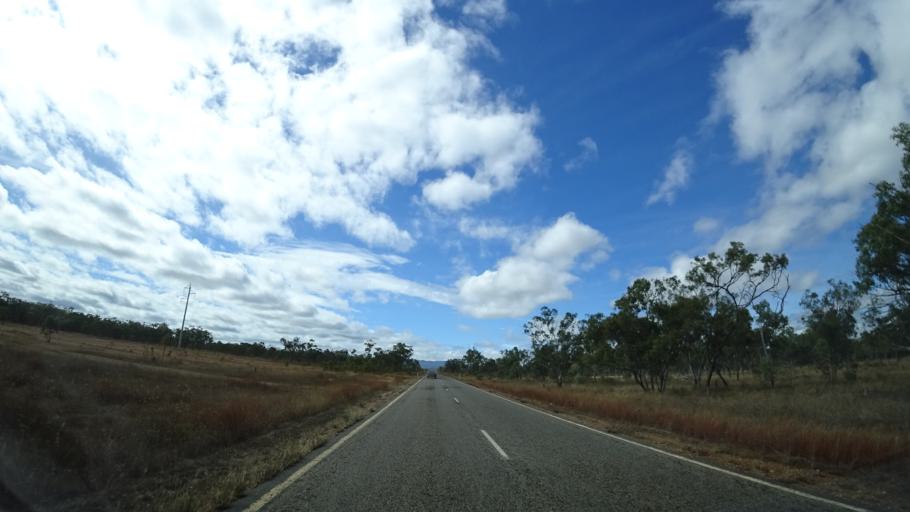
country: AU
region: Queensland
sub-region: Cairns
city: Port Douglas
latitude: -16.4972
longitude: 144.9846
